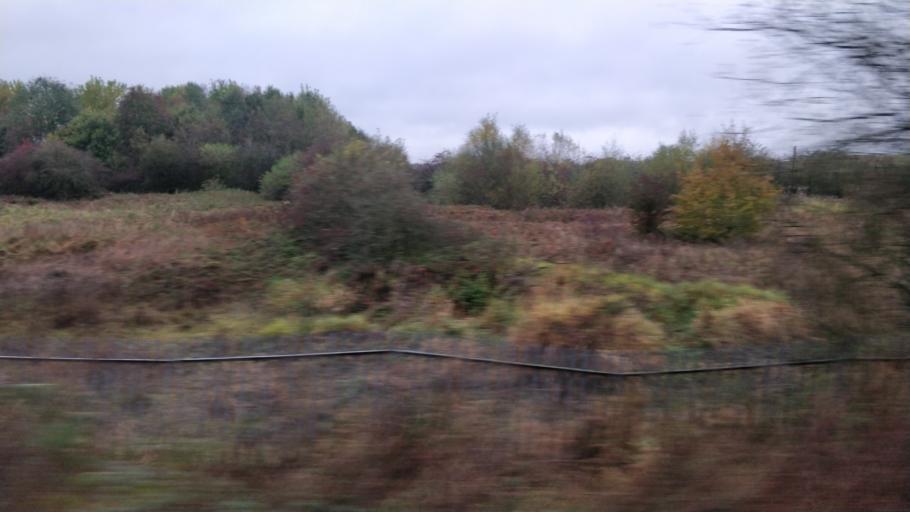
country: GB
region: England
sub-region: Borough of Wigan
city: Tyldesley
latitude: 53.5285
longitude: -2.4678
